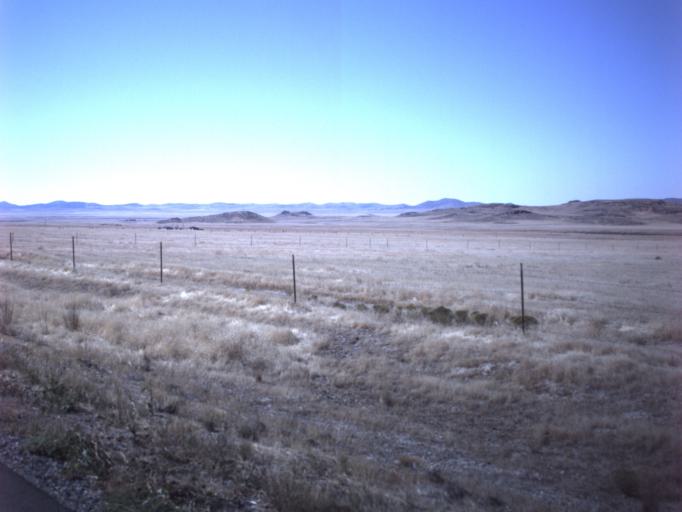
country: US
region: Utah
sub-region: Tooele County
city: Grantsville
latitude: 40.4057
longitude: -112.7482
